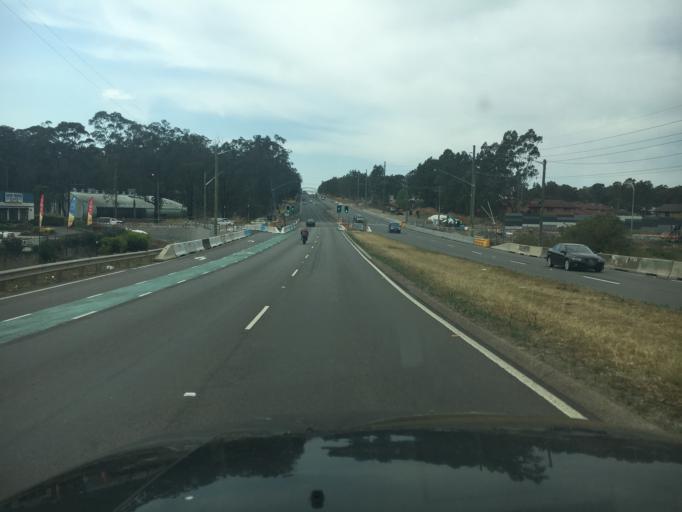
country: AU
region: New South Wales
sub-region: Maitland Municipality
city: East Maitland
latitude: -32.7614
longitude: 151.5951
